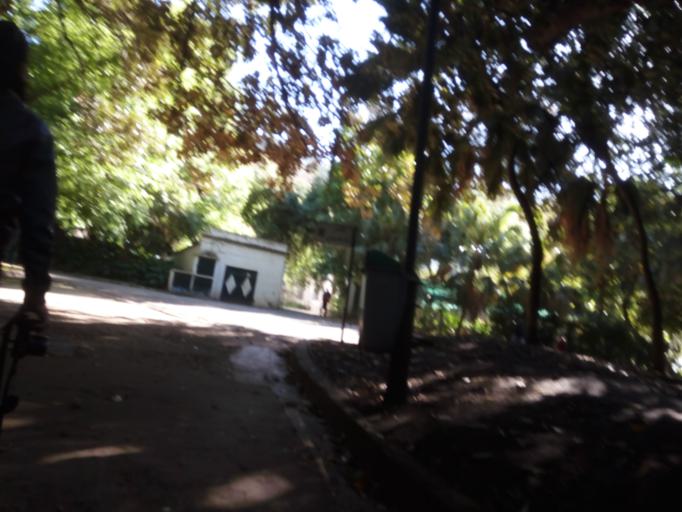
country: DZ
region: Alger
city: Algiers
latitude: 36.7459
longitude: 3.0758
